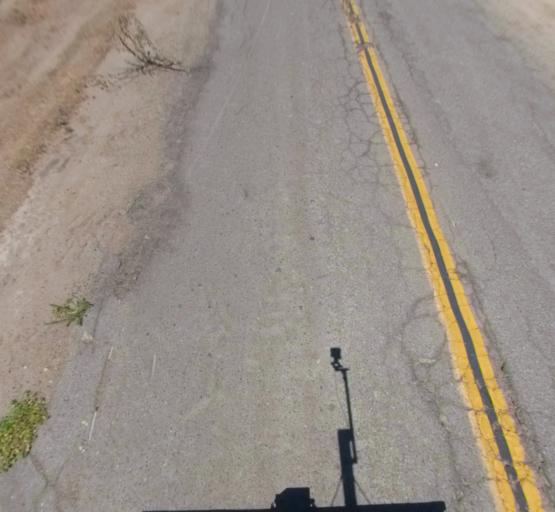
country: US
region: California
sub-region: Madera County
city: Chowchilla
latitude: 37.0545
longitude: -120.4184
